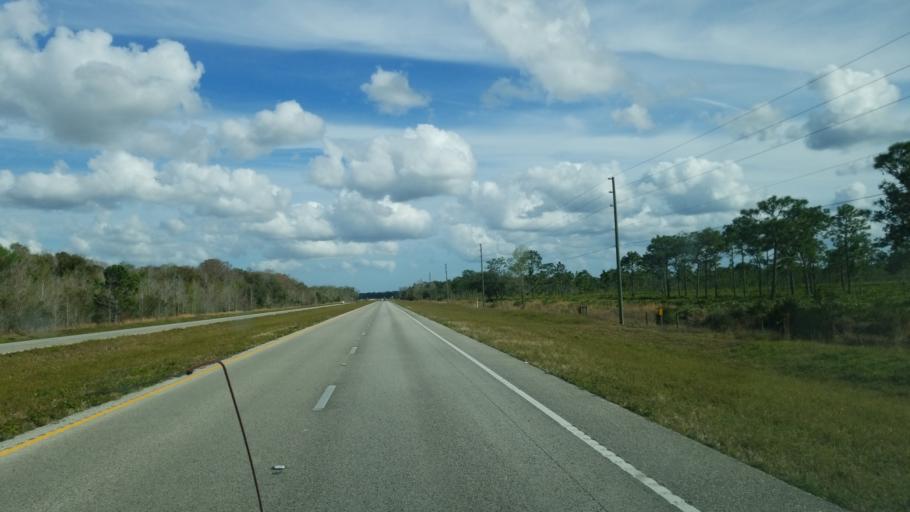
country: US
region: Florida
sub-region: Osceola County
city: Saint Cloud
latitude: 28.1357
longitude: -81.0297
